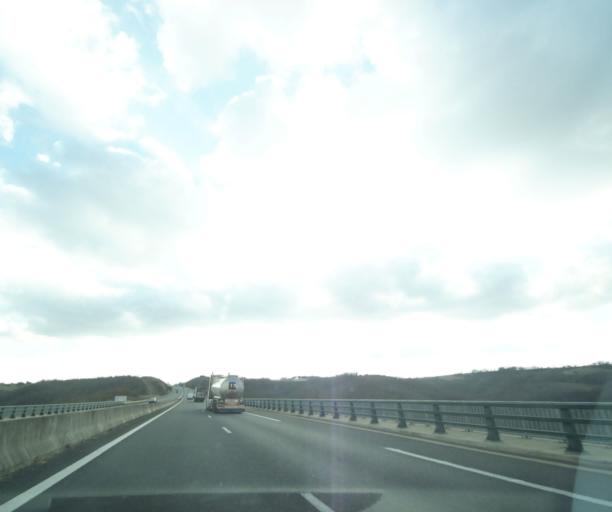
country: FR
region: Midi-Pyrenees
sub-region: Departement du Lot
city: Cahors
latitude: 44.5428
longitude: 1.5152
